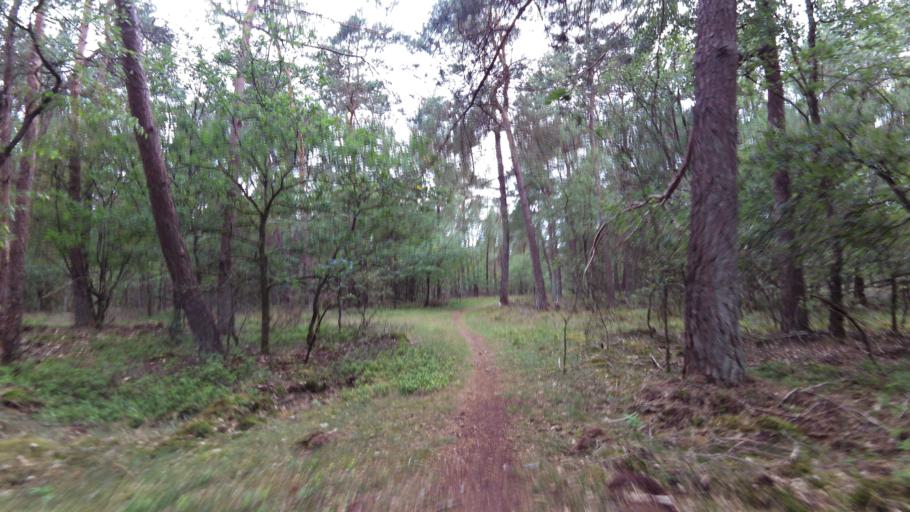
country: NL
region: Gelderland
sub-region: Gemeente Apeldoorn
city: Uddel
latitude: 52.2215
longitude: 5.8025
